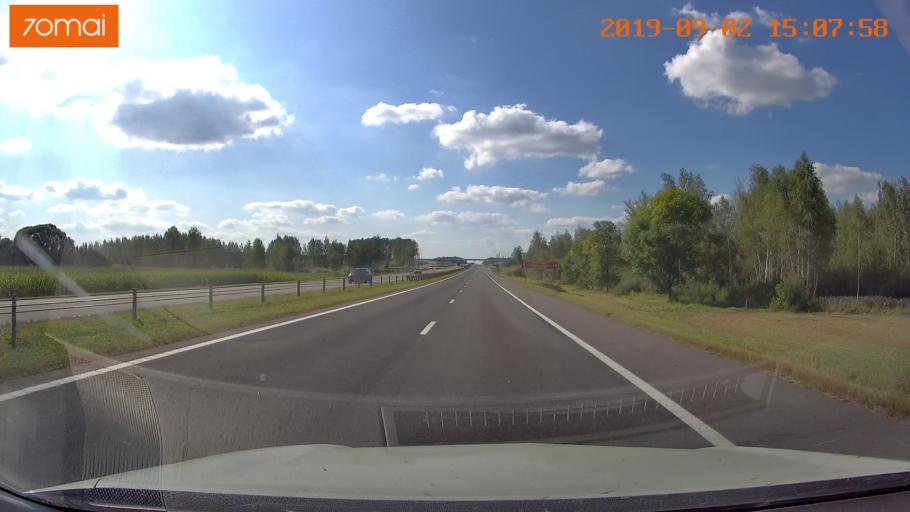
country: BY
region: Mogilev
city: Vishow
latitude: 53.9841
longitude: 29.8575
